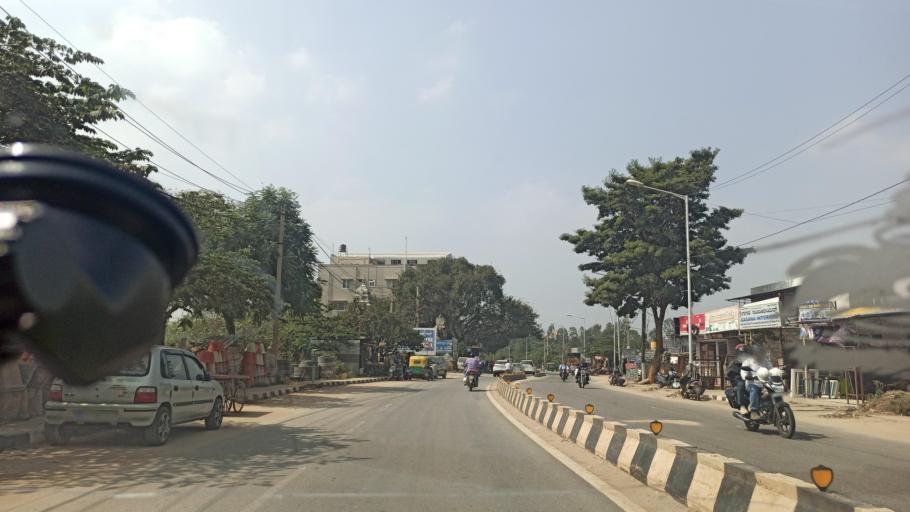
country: IN
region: Karnataka
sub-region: Bangalore Urban
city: Yelahanka
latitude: 13.1039
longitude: 77.6139
